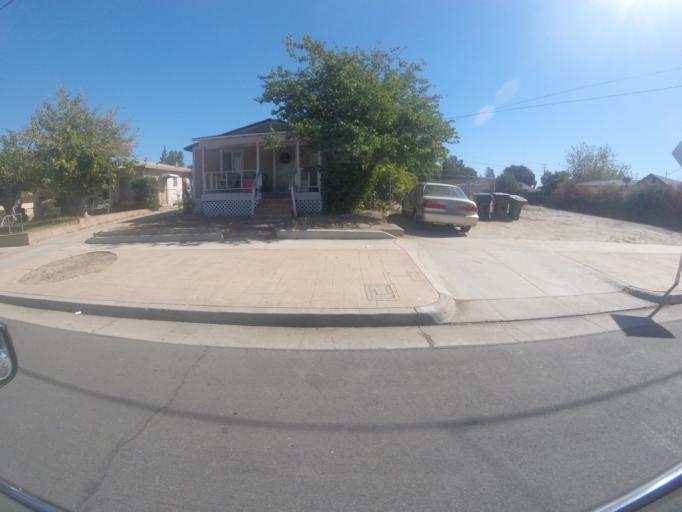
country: US
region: California
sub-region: San Bernardino County
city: Redlands
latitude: 34.0681
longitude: -117.1792
